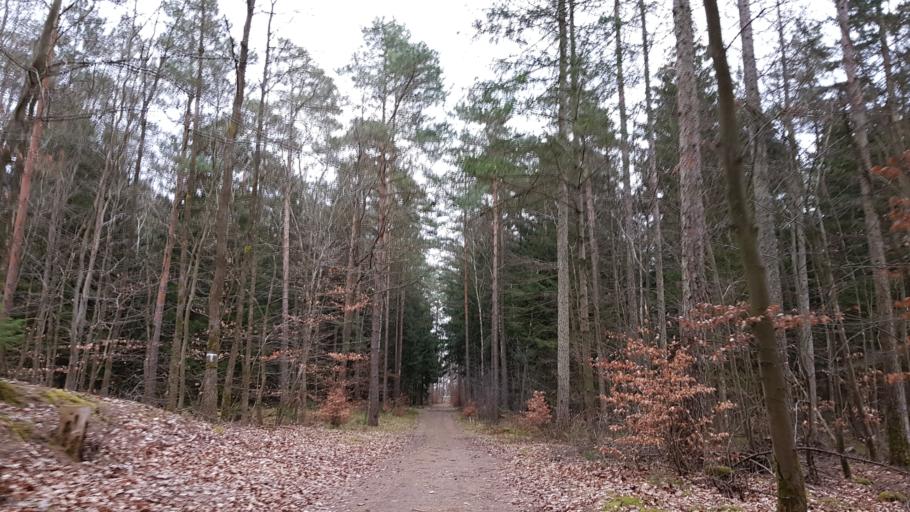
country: DE
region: Lower Saxony
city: Deutsch Evern
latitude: 53.2220
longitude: 10.4337
